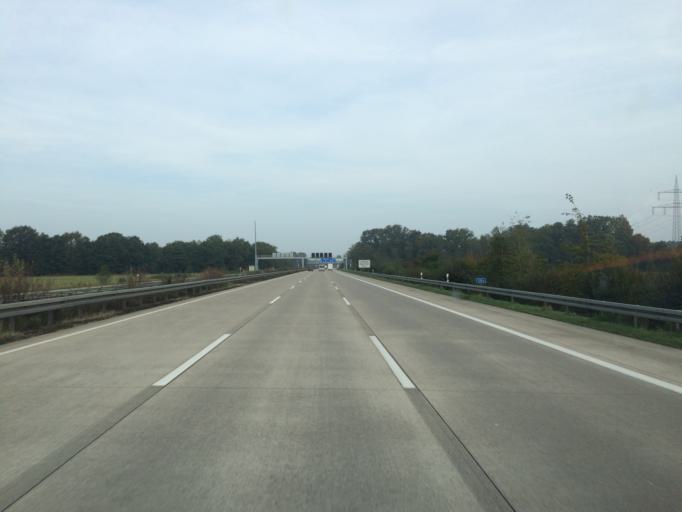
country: DE
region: Lower Saxony
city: Isernhagen Farster Bauerschaft
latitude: 52.5357
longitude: 9.8055
